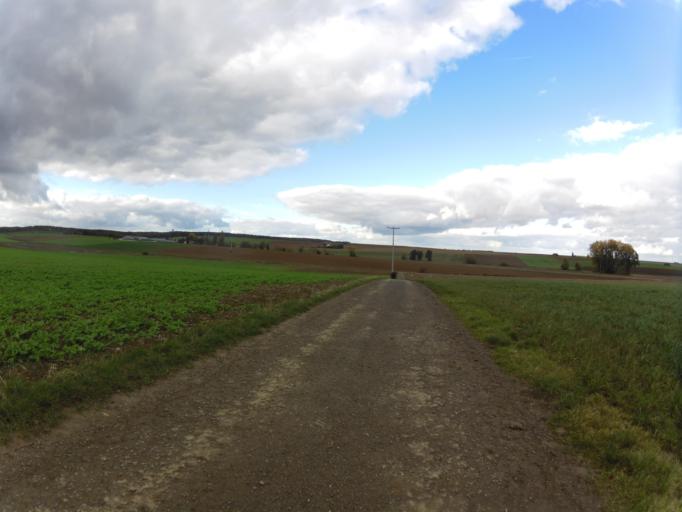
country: DE
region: Bavaria
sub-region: Regierungsbezirk Unterfranken
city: Unterpleichfeld
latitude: 49.8783
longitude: 10.0191
